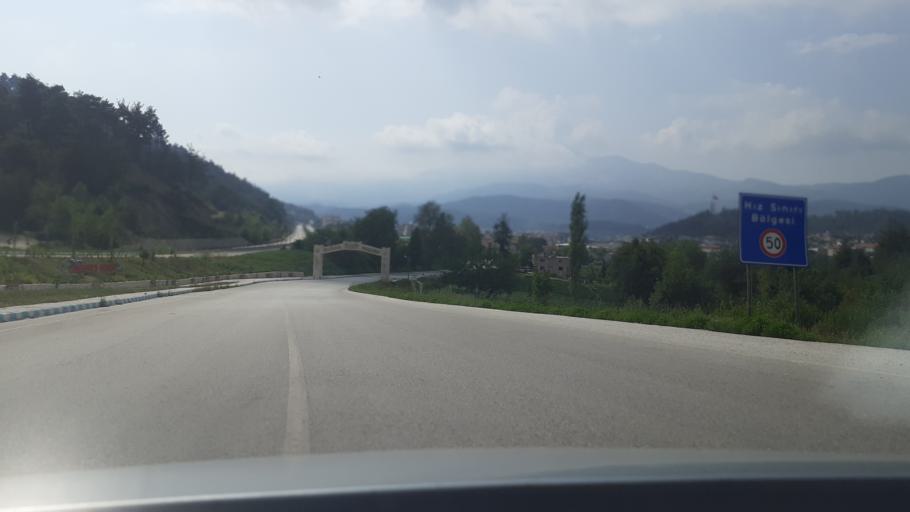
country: TR
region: Hatay
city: Yayladagi
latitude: 35.8965
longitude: 36.0781
